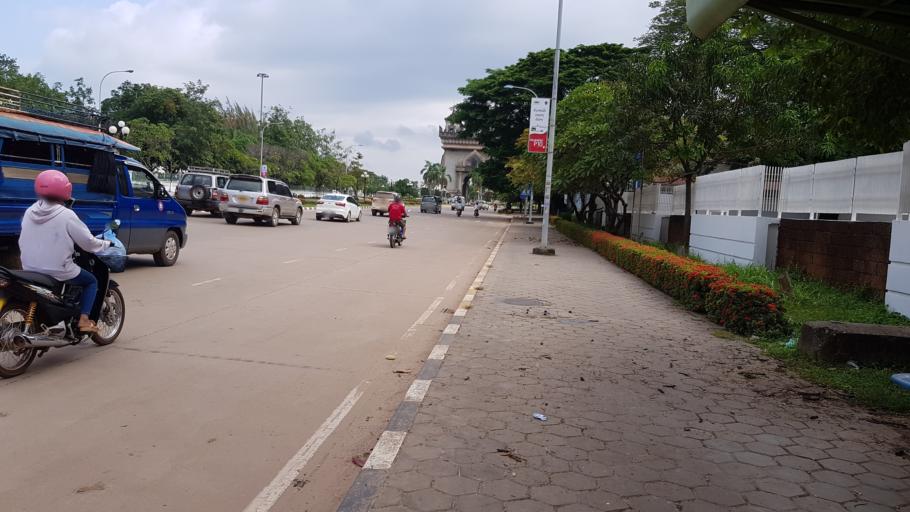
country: LA
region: Vientiane
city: Vientiane
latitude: 17.9689
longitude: 102.6170
